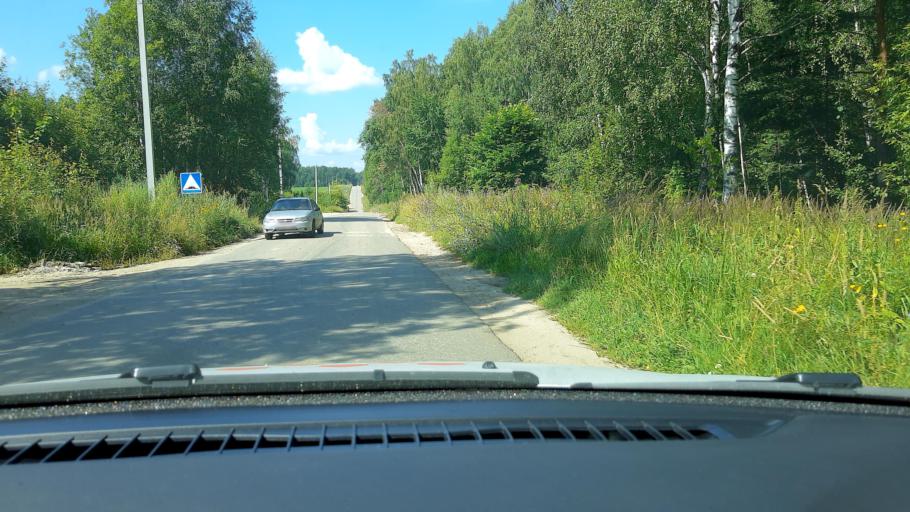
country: RU
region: Nizjnij Novgorod
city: Burevestnik
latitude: 56.0519
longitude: 43.9661
